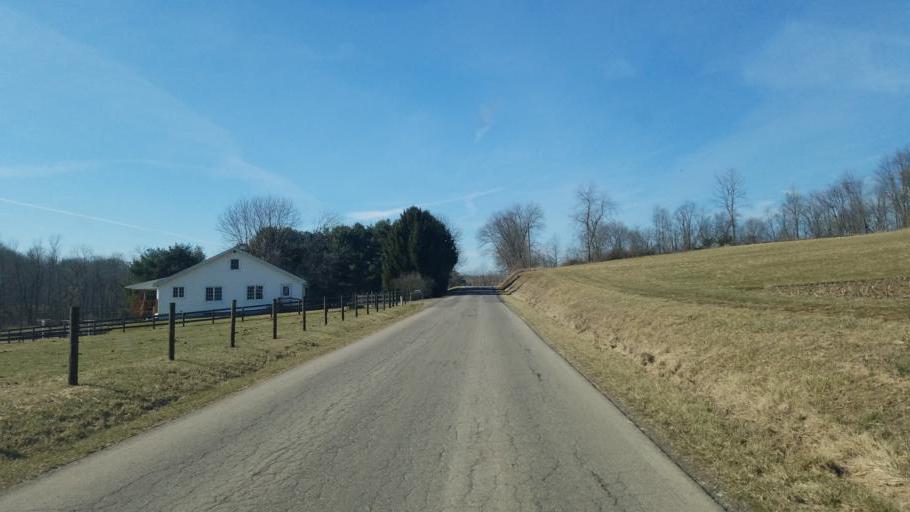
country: US
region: Ohio
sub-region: Knox County
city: Danville
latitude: 40.5369
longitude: -82.3181
